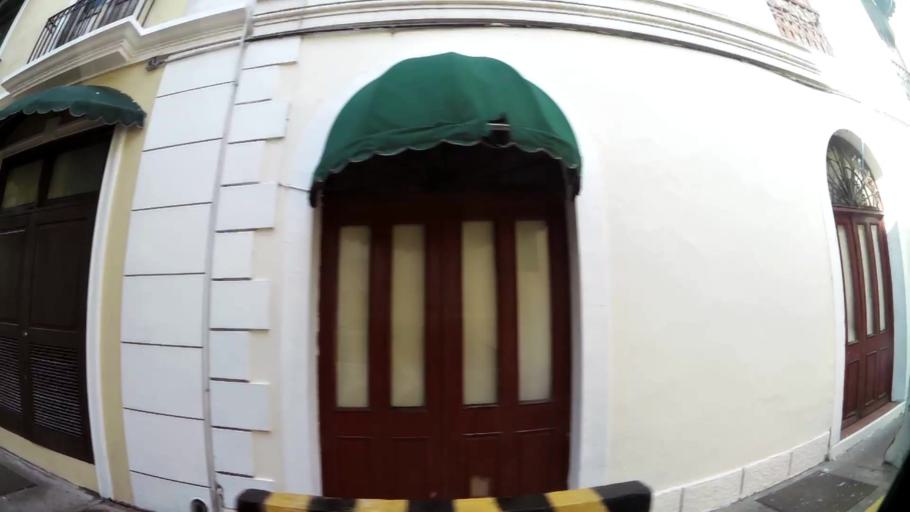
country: PA
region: Panama
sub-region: Distrito de Panama
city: Ancon
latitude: 8.9538
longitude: -79.5337
